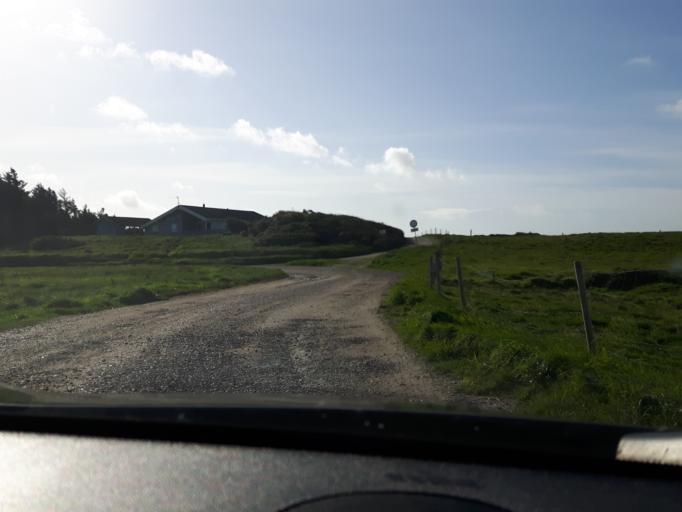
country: DK
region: North Denmark
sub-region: Hjorring Kommune
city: Hjorring
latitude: 57.4627
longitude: 9.7881
